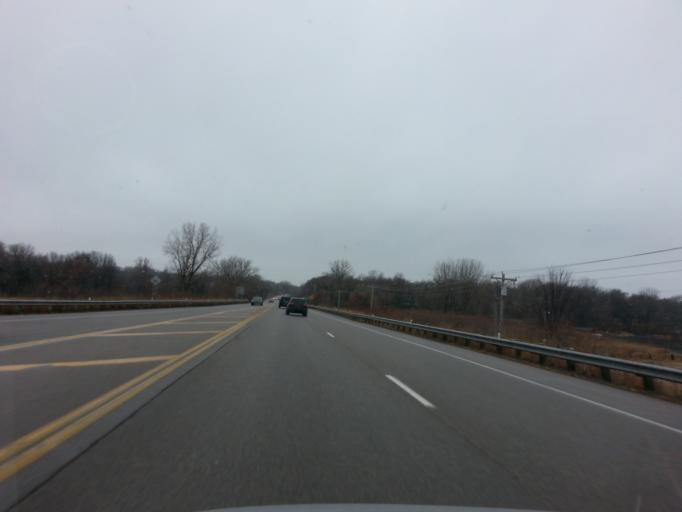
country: US
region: Minnesota
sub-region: Scott County
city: Prior Lake
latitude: 44.7401
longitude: -93.3814
